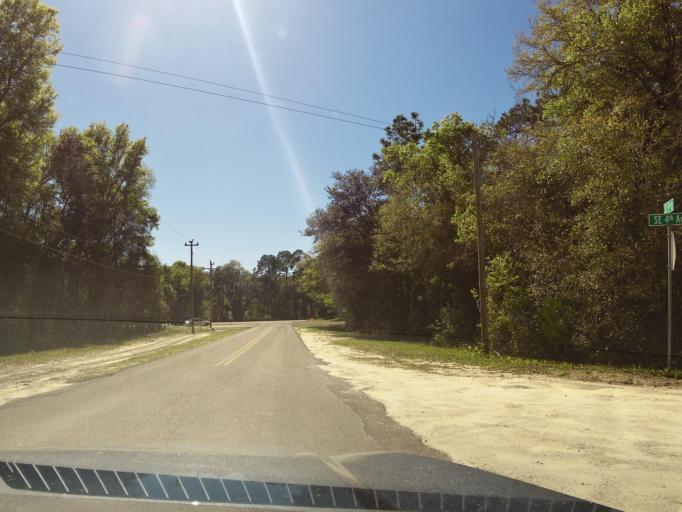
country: US
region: Florida
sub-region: Clay County
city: Keystone Heights
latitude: 29.7998
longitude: -82.0518
